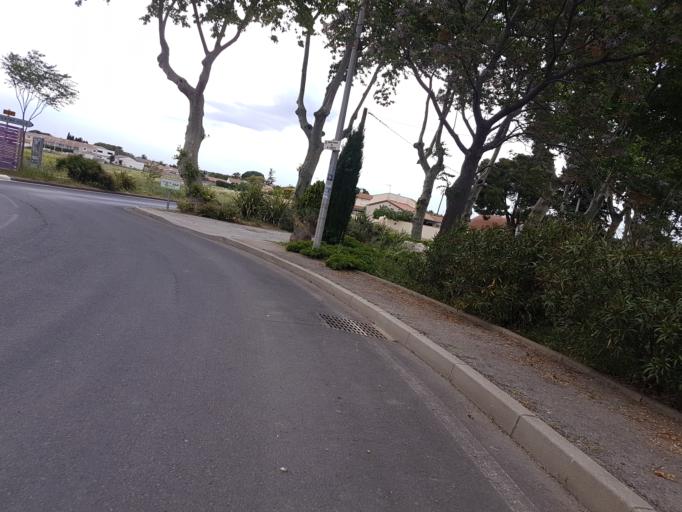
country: FR
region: Languedoc-Roussillon
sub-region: Departement de l'Herault
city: Cers
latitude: 43.3194
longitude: 3.3032
